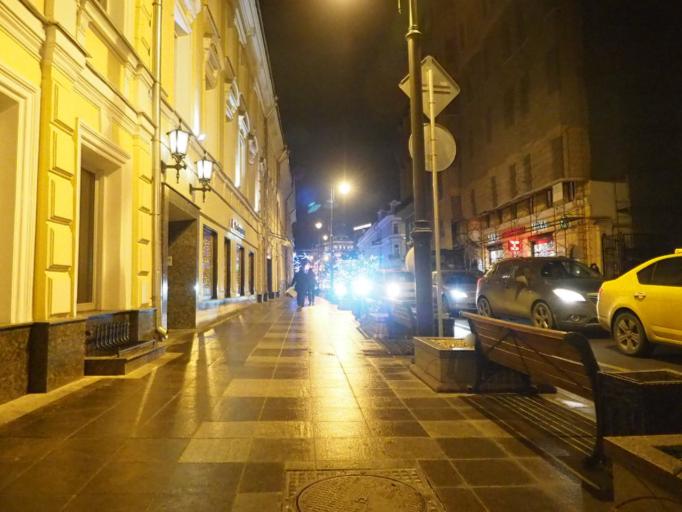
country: RU
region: Moscow
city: Moscow
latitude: 55.7613
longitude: 37.6148
